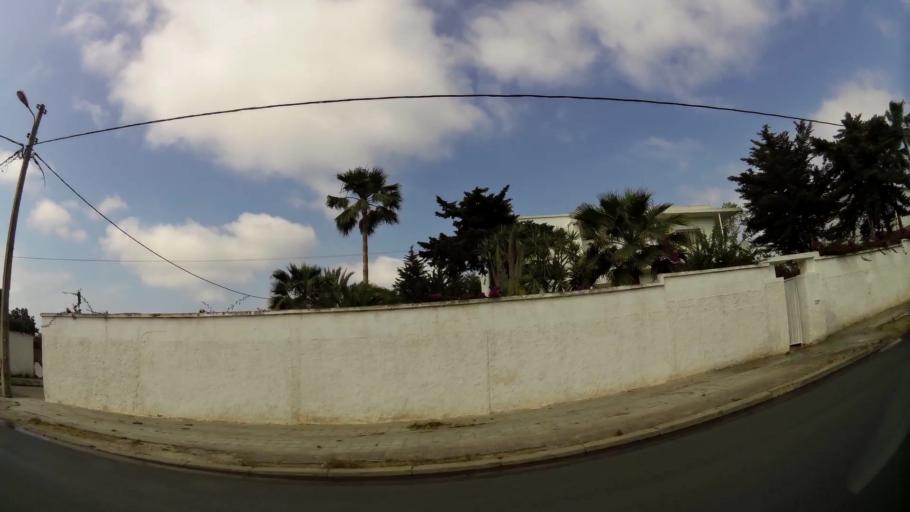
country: MA
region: Rabat-Sale-Zemmour-Zaer
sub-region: Rabat
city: Rabat
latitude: 33.9749
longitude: -6.8461
